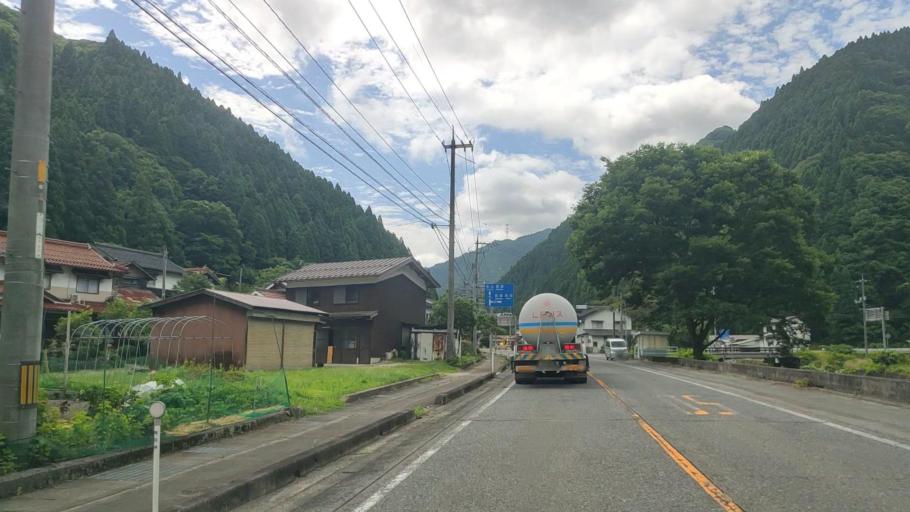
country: JP
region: Tottori
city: Yonago
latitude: 35.2284
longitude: 133.4441
